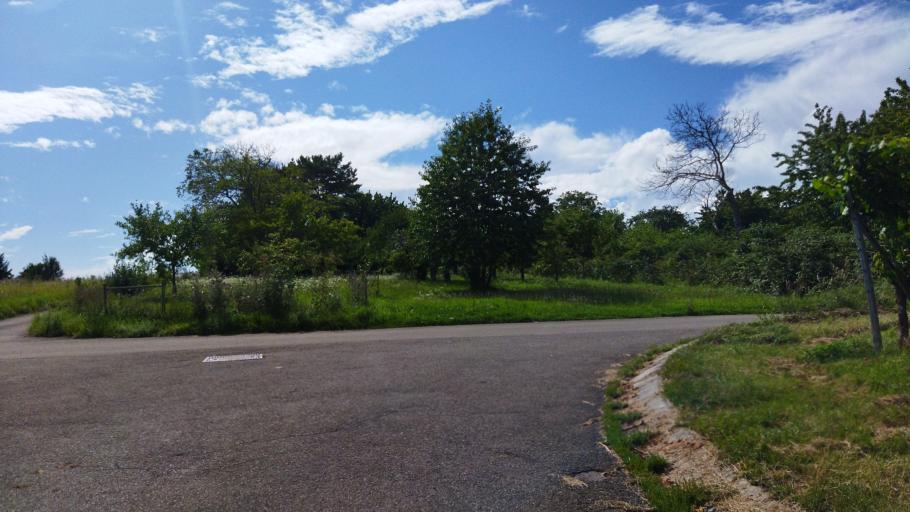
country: DE
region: Baden-Wuerttemberg
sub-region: Regierungsbezirk Stuttgart
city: Bonnigheim
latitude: 49.0311
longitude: 9.0828
